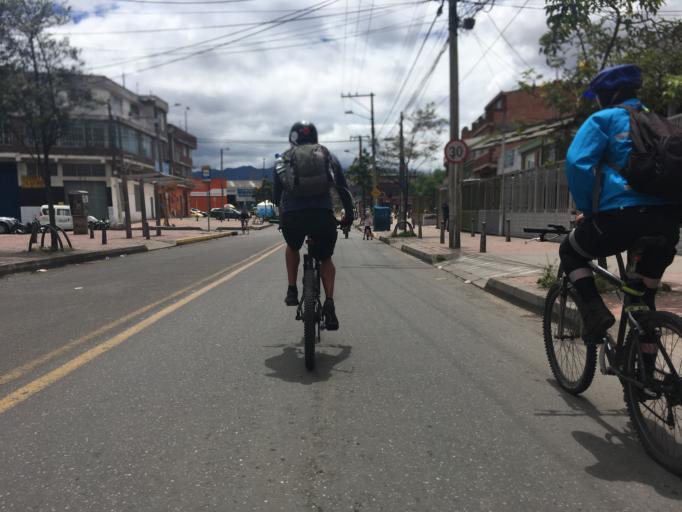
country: CO
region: Bogota D.C.
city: Bogota
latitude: 4.6068
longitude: -74.1429
